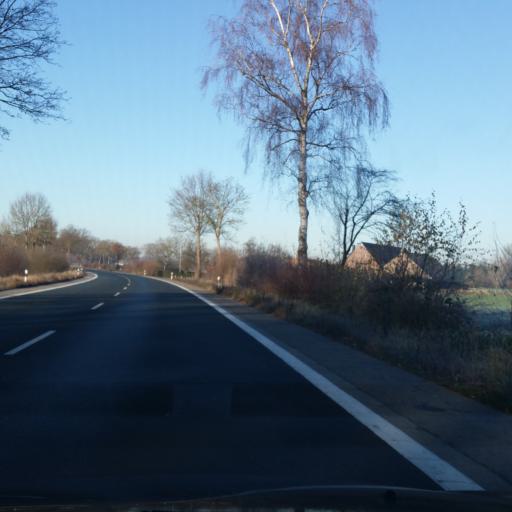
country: DE
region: North Rhine-Westphalia
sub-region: Regierungsbezirk Munster
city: Isselburg
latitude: 51.8175
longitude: 6.4684
